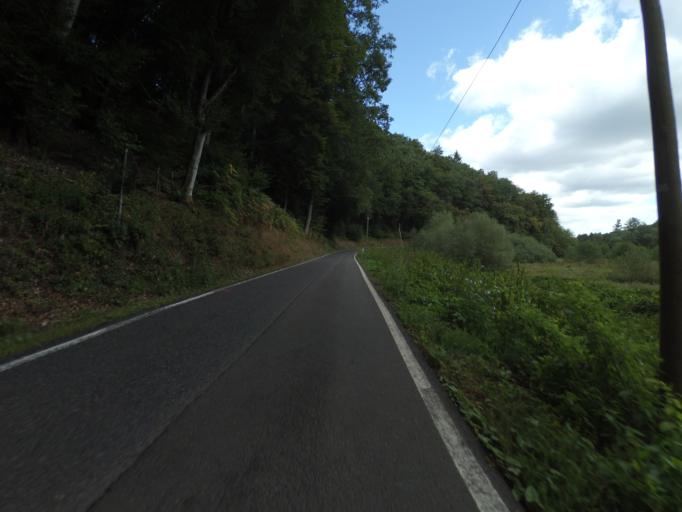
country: DE
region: Rheinland-Pfalz
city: Trassem
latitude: 49.5552
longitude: 6.5151
